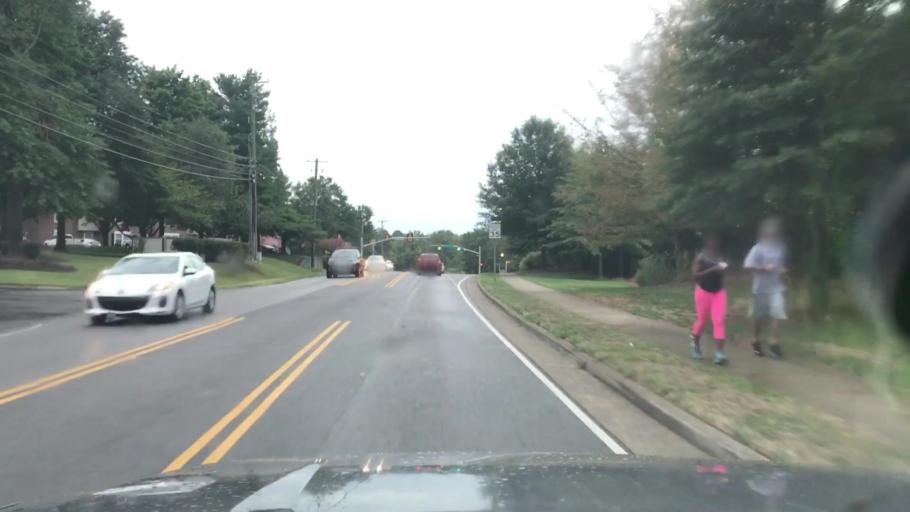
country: US
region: Tennessee
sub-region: Davidson County
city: Lakewood
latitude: 36.1694
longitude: -86.6150
